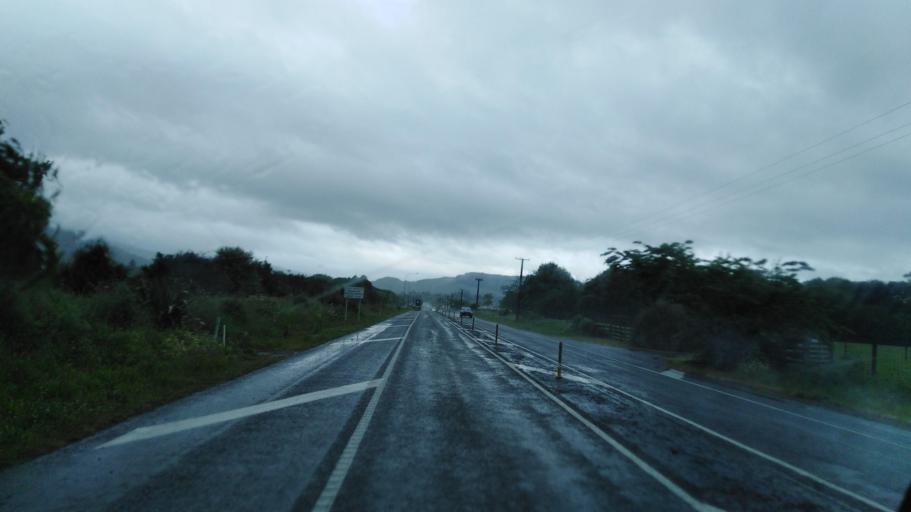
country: NZ
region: Wellington
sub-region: Kapiti Coast District
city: Otaki
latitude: -40.7066
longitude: 175.2199
